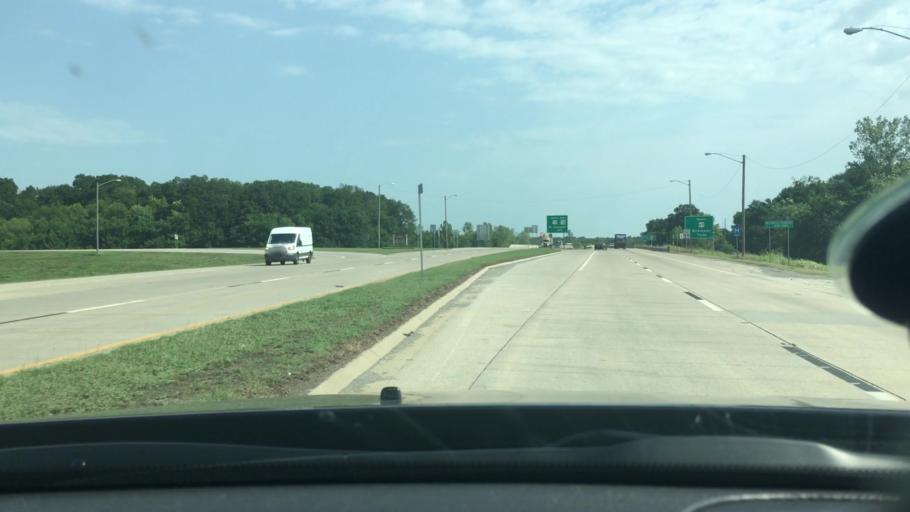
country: US
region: Oklahoma
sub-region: Atoka County
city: Atoka
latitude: 34.3916
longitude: -96.1259
